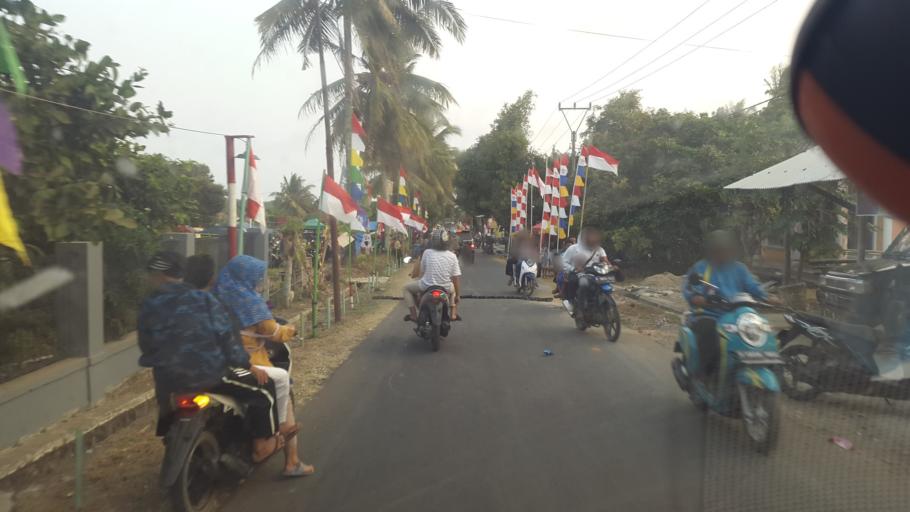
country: ID
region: West Java
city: Cikujang
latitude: -7.3647
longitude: 106.5647
